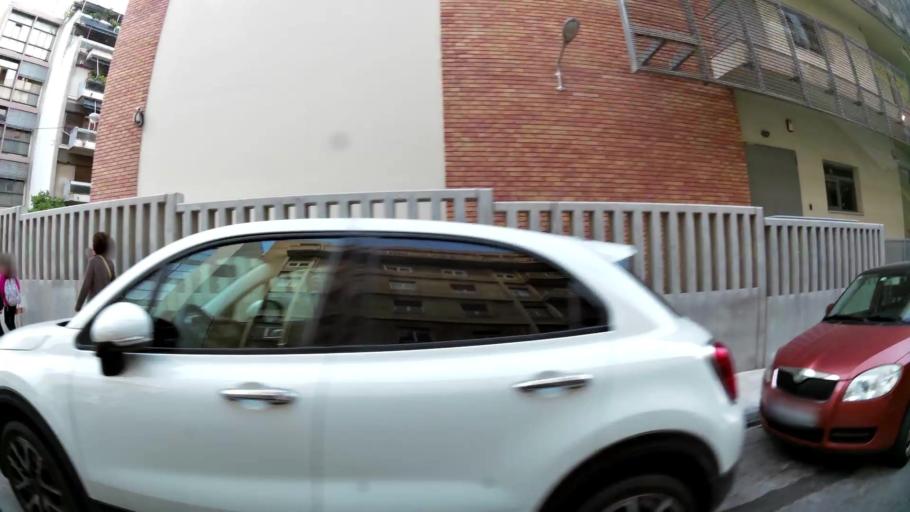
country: GR
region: Attica
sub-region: Nomarchia Athinas
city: Kaisariani
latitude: 37.9850
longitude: 23.7571
